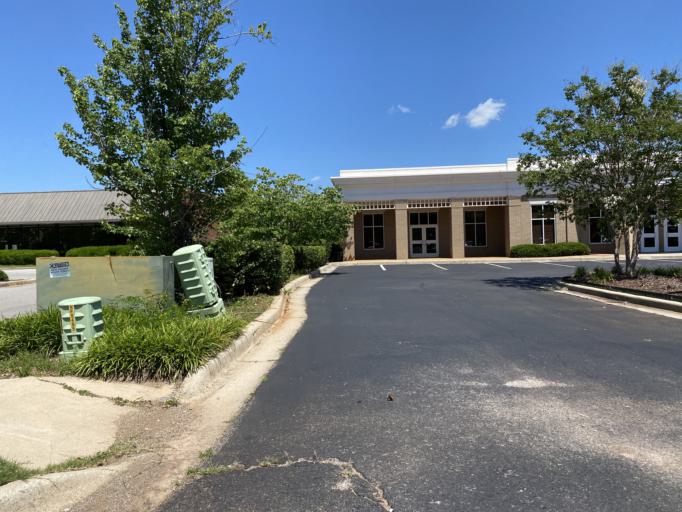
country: US
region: Alabama
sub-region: Madison County
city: Redstone Arsenal
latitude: 34.7403
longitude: -86.6562
